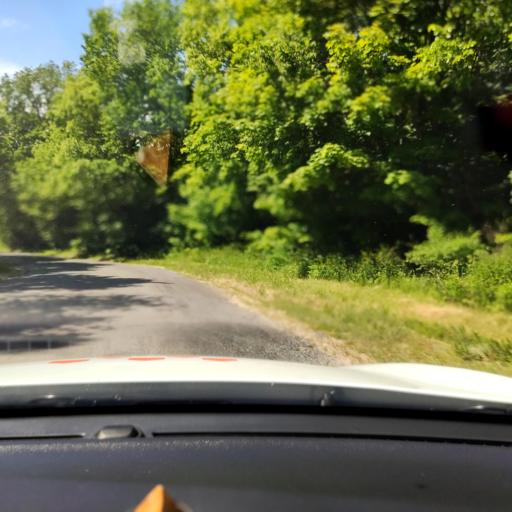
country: RU
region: Tatarstan
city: Osinovo
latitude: 55.7799
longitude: 48.8046
